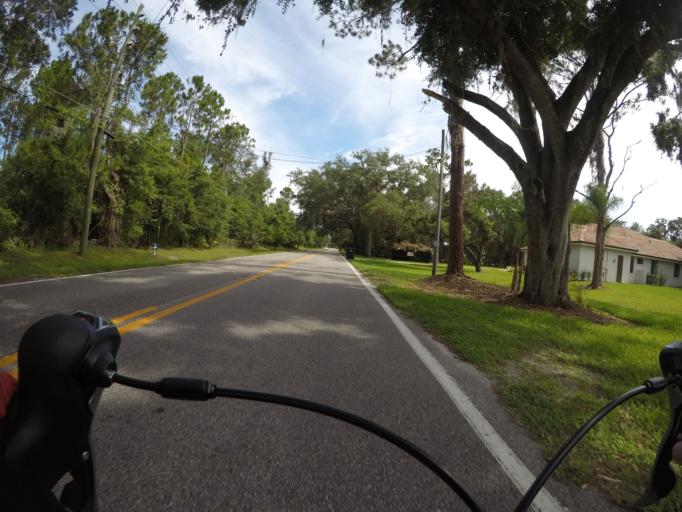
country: US
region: Florida
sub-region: Osceola County
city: Buenaventura Lakes
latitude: 28.3923
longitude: -81.2279
